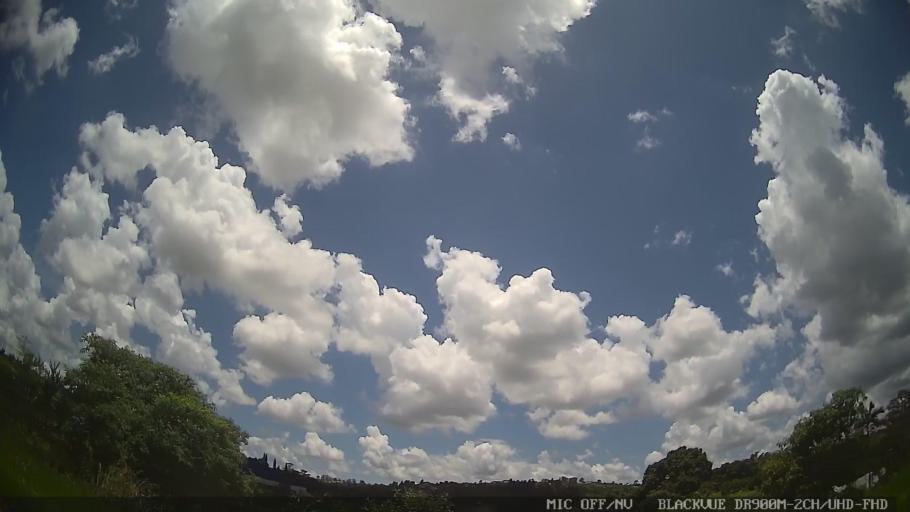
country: BR
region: Sao Paulo
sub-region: Serra Negra
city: Serra Negra
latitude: -22.6276
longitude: -46.7218
